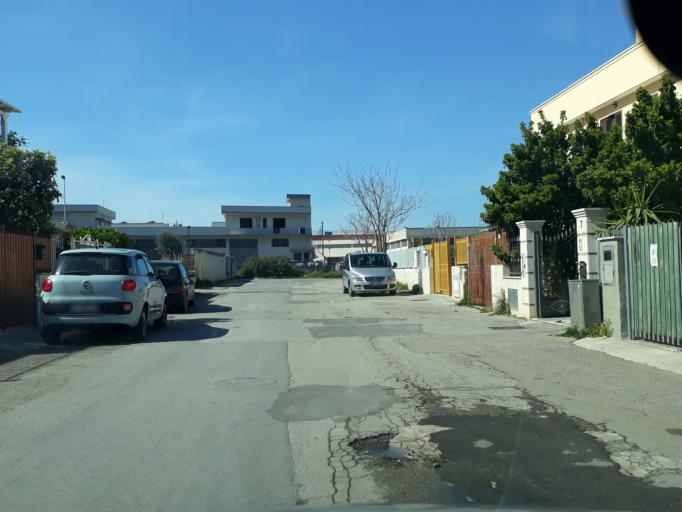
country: IT
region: Apulia
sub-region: Provincia di Brindisi
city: Fasano
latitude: 40.8421
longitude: 17.3541
